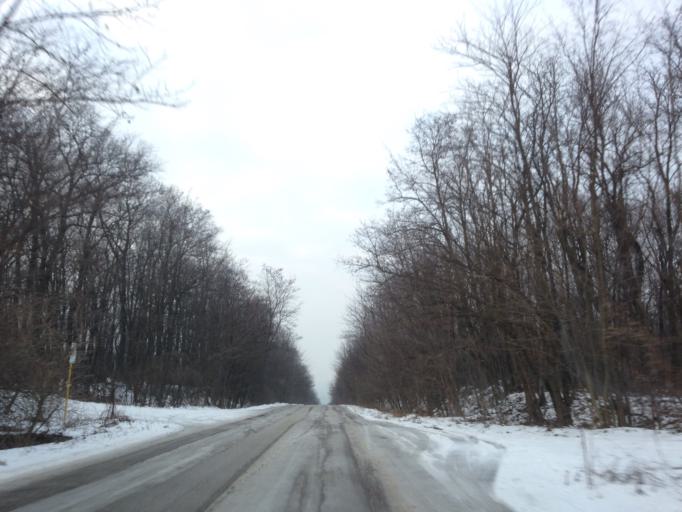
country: SK
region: Nitriansky
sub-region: Okres Nitra
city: Vrable
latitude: 48.0955
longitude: 18.3653
